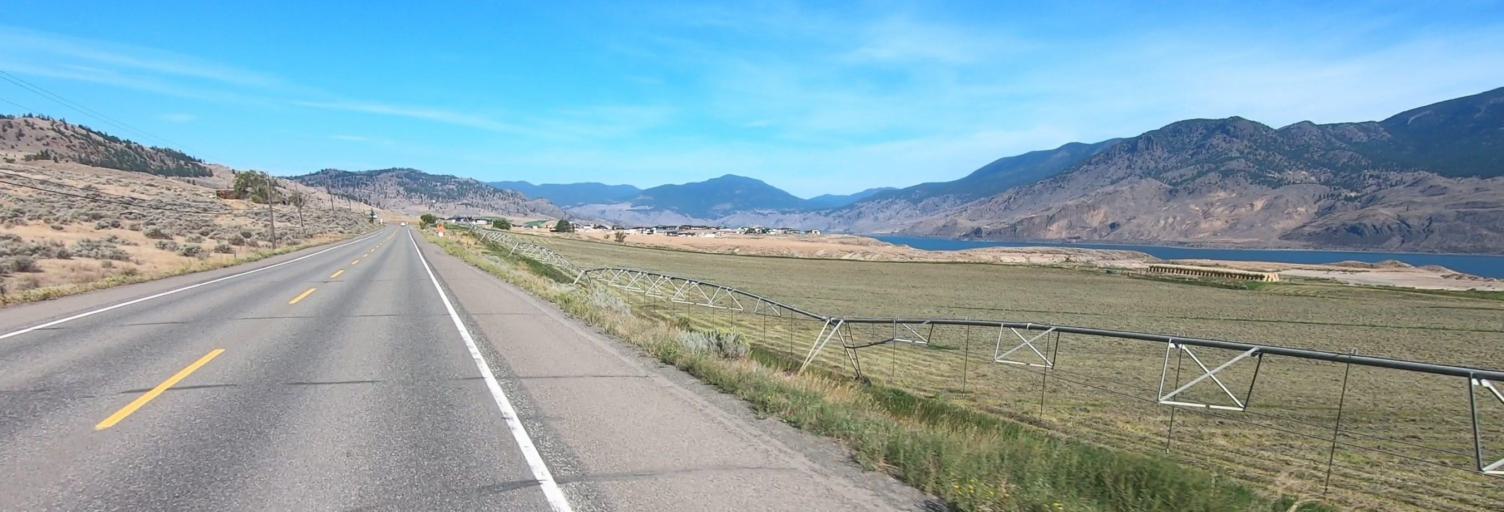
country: CA
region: British Columbia
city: Logan Lake
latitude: 50.7221
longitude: -120.6619
